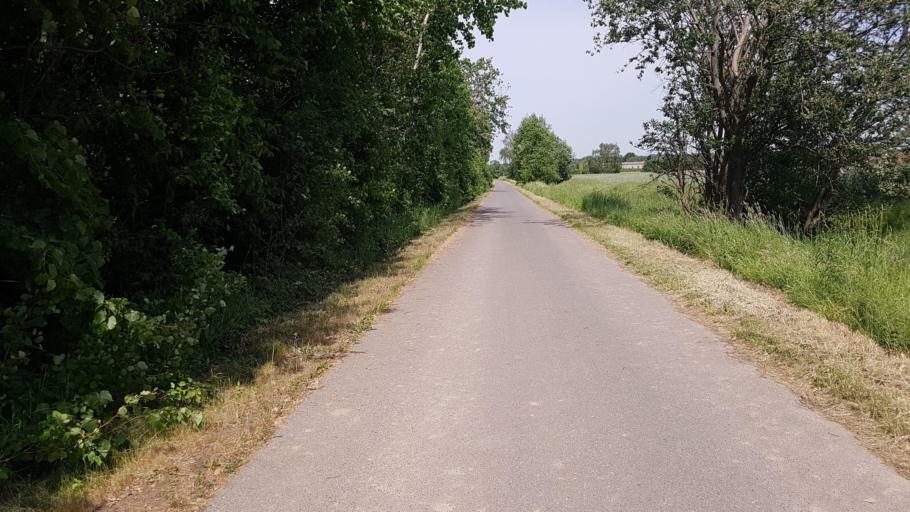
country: DE
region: Brandenburg
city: Grosskmehlen
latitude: 51.3780
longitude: 13.7087
